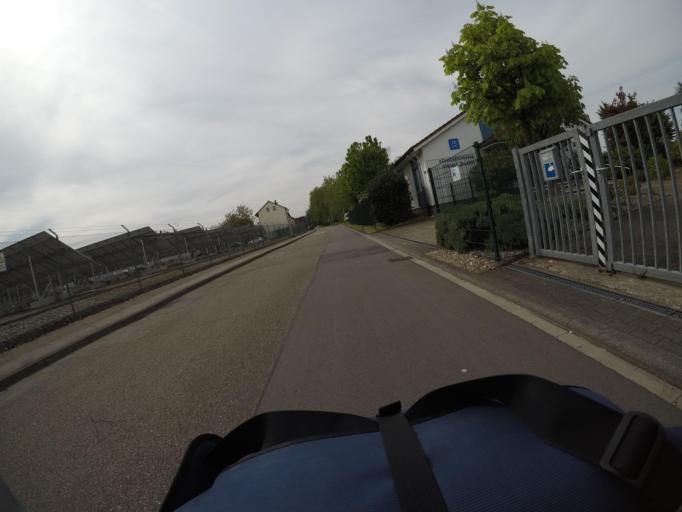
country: DE
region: Baden-Wuerttemberg
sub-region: Karlsruhe Region
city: Rastatt
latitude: 48.8537
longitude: 8.2206
